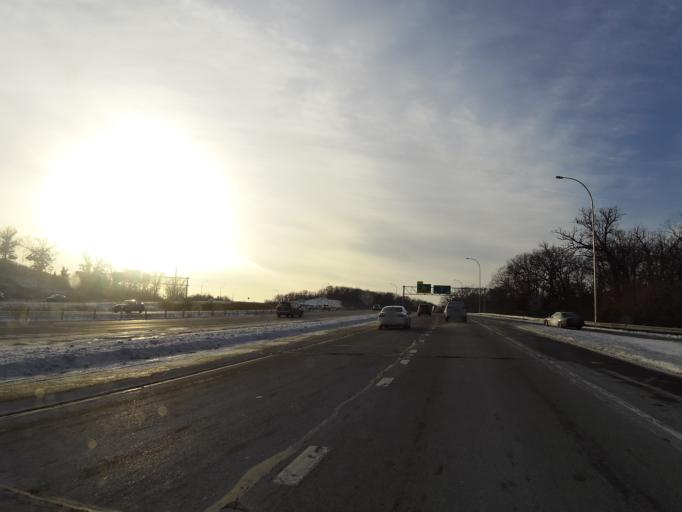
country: US
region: Minnesota
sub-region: Hennepin County
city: Edina
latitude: 44.8908
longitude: -93.4017
